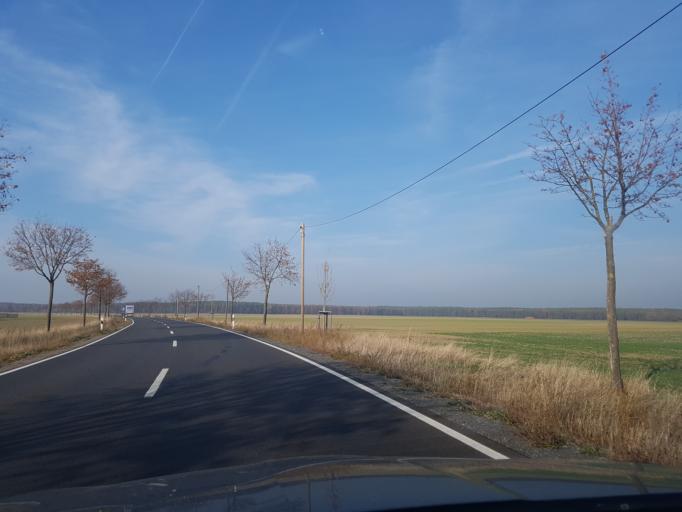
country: DE
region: Saxony
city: Arzberg
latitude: 51.5492
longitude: 13.1553
